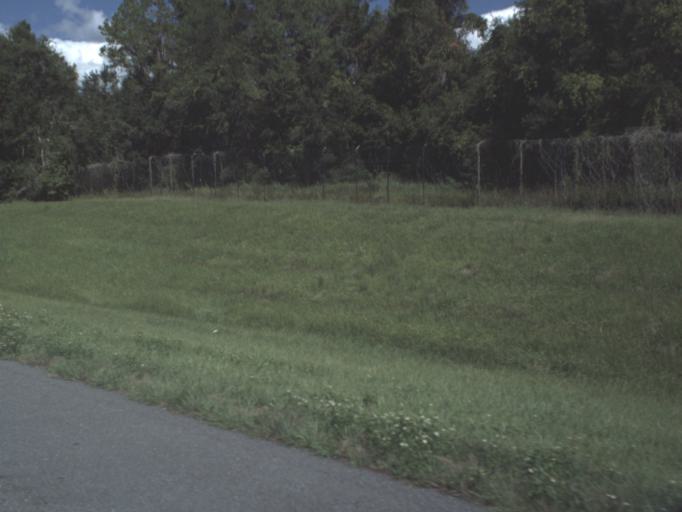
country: US
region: Florida
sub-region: Hernando County
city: Brookridge
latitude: 28.6389
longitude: -82.4890
